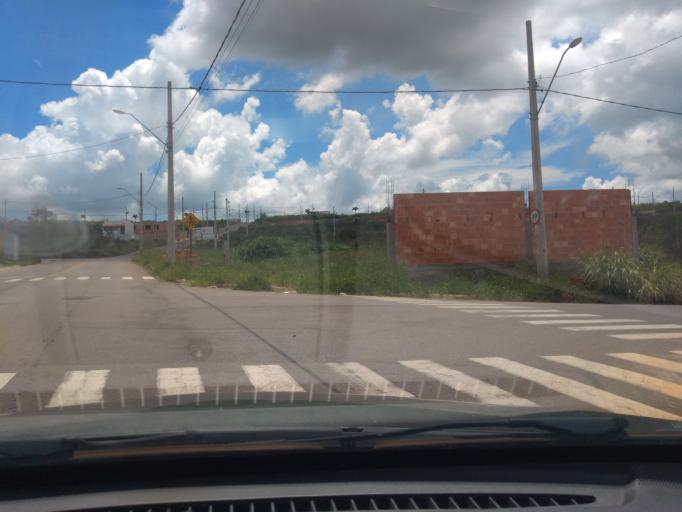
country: BR
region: Minas Gerais
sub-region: Tres Coracoes
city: Tres Coracoes
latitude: -21.6811
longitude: -45.2754
